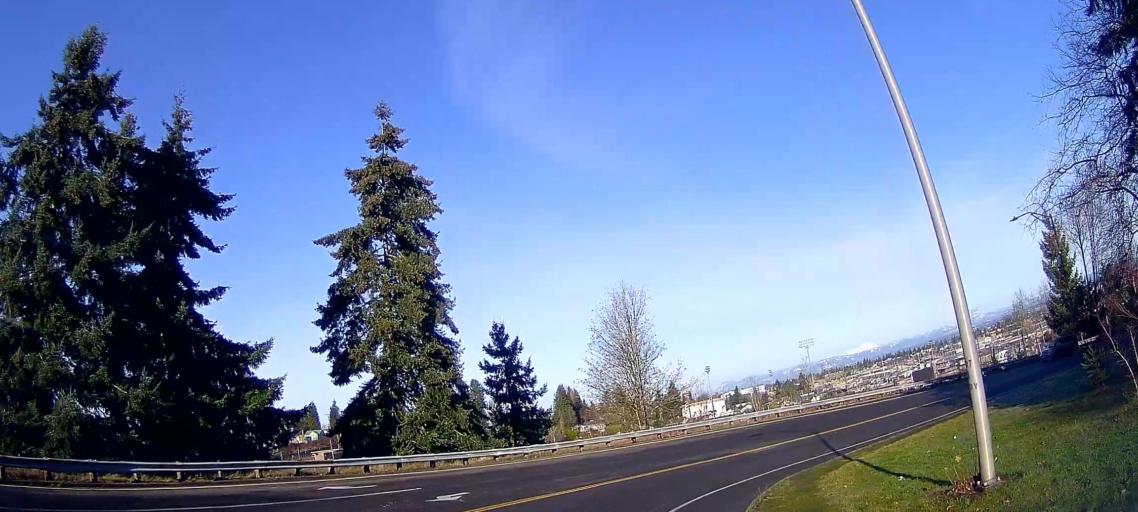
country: US
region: Washington
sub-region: Snohomish County
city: Everett
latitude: 47.9643
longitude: -122.2038
